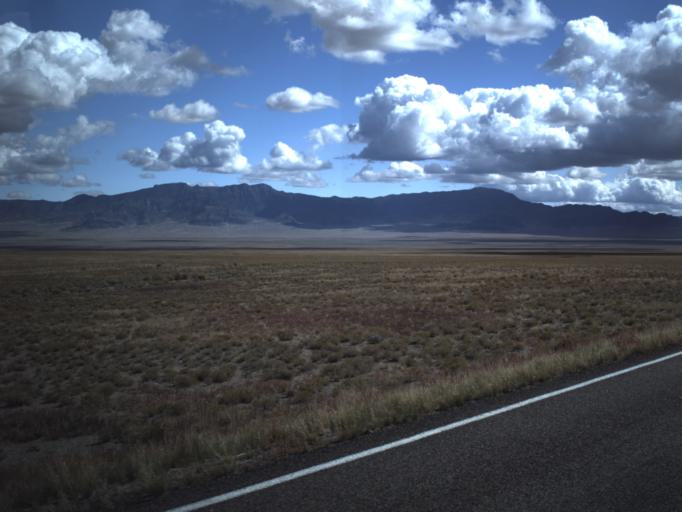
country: US
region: Utah
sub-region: Beaver County
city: Milford
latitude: 38.5784
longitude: -113.8047
